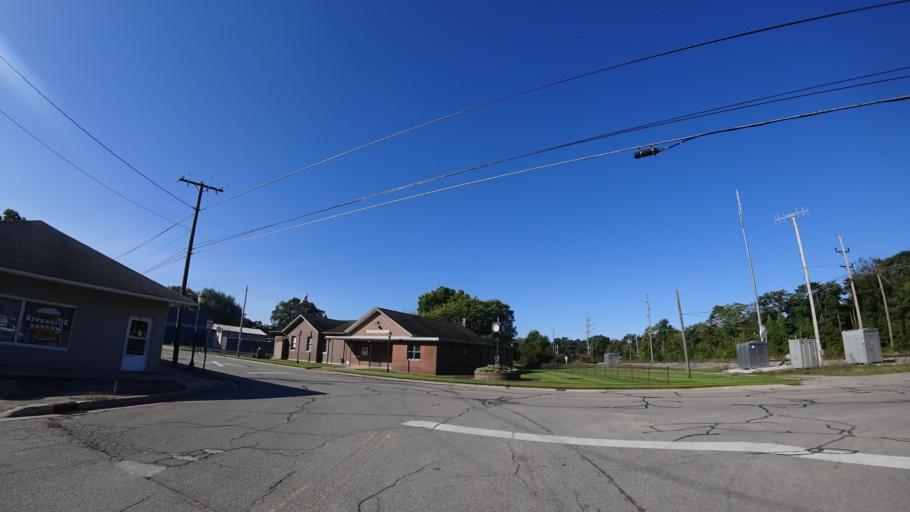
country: US
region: Michigan
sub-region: Berrien County
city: Lake Michigan Beach
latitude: 42.1830
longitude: -86.3833
